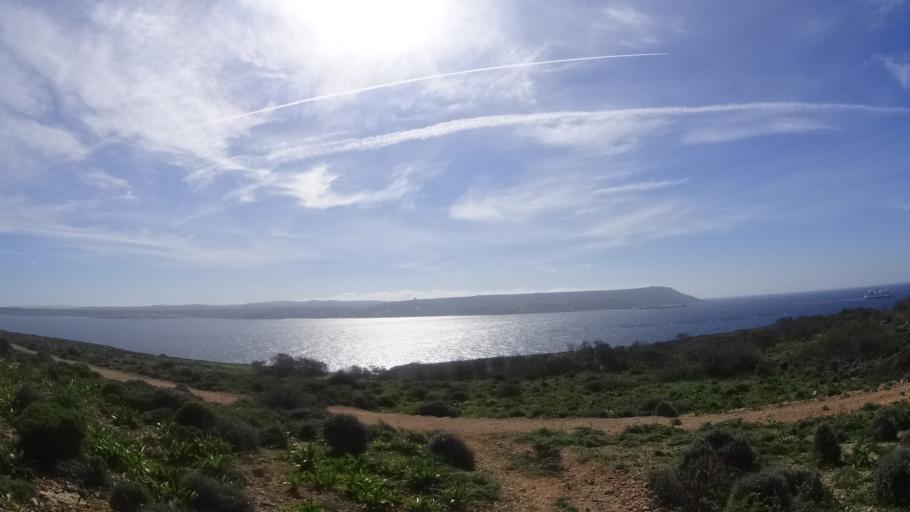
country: MT
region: Il-Qala
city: Qala
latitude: 36.0073
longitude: 14.3344
